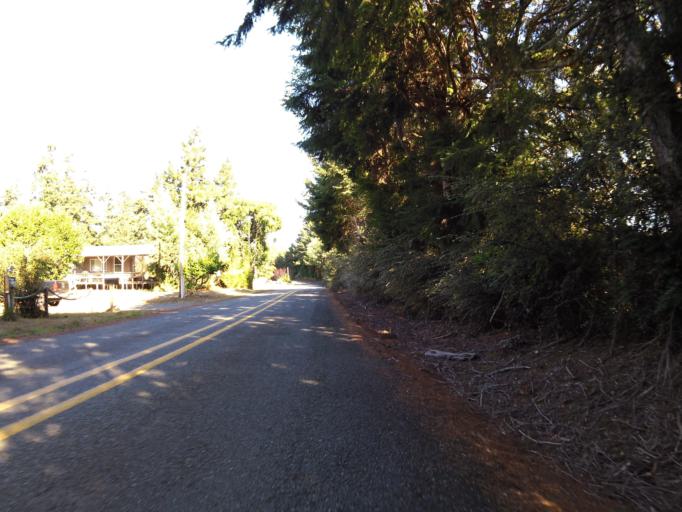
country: US
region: Oregon
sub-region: Coos County
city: Bandon
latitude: 43.0394
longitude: -124.4055
